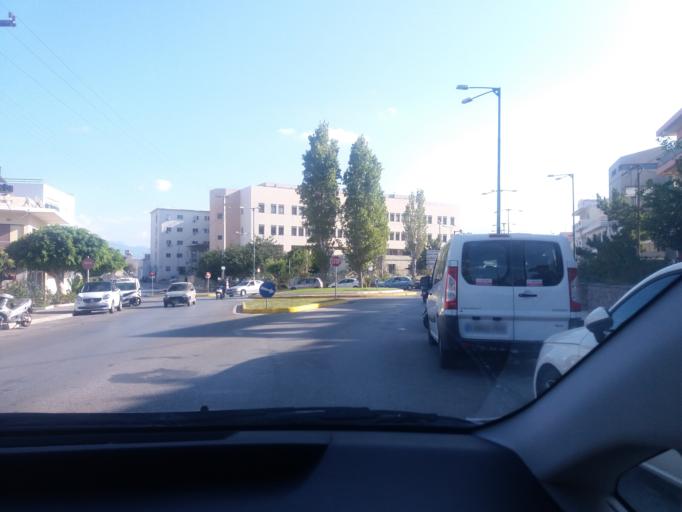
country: GR
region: Crete
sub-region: Nomos Lasithiou
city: Agios Nikolaos
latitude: 35.1955
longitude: 25.7128
